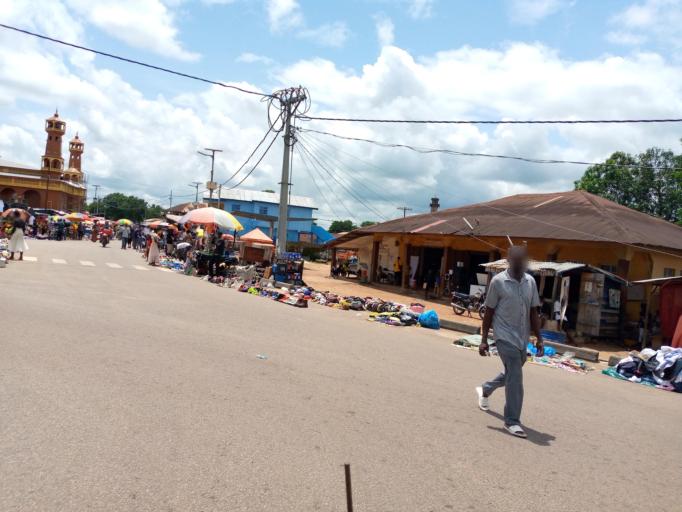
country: SL
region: Northern Province
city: Magburaka
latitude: 8.7234
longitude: -11.9490
